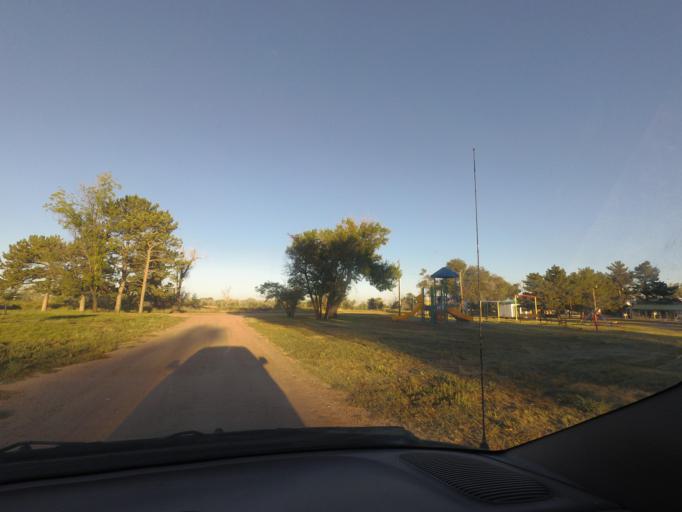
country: US
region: Colorado
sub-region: Yuma County
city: Yuma
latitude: 39.6638
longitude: -102.8516
